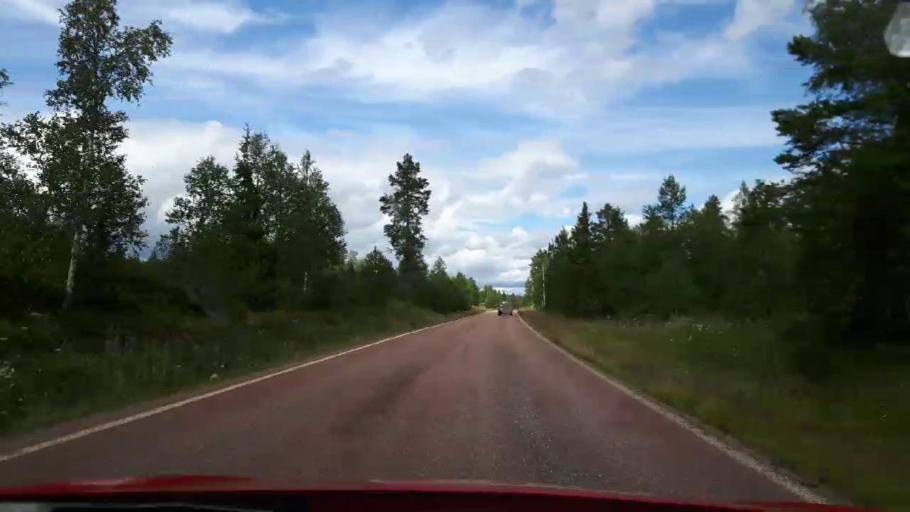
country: NO
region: Hedmark
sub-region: Trysil
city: Innbygda
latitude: 62.0019
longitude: 12.9773
